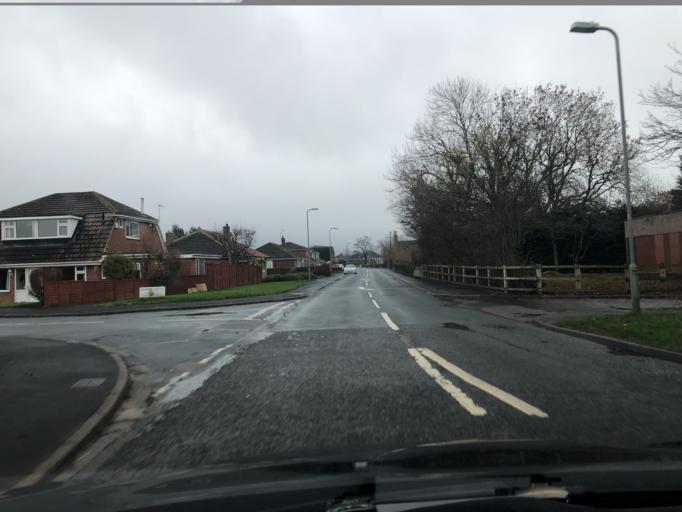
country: GB
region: England
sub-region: North Yorkshire
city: Stokesley
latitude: 54.4771
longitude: -1.1875
